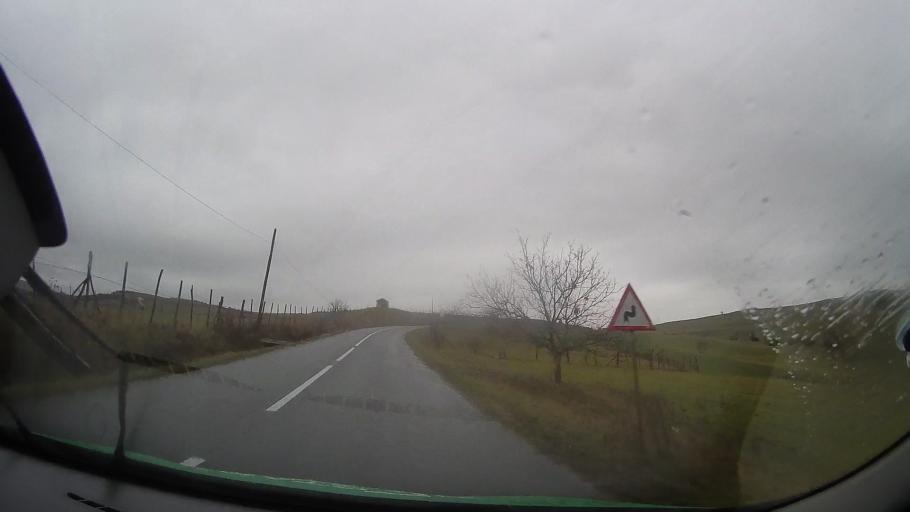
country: RO
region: Bistrita-Nasaud
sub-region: Comuna Monor
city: Monor
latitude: 46.9548
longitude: 24.6770
